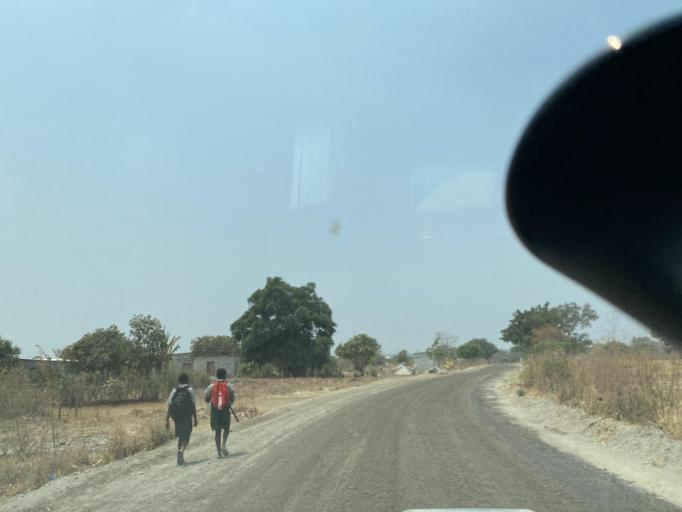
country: ZM
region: Lusaka
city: Lusaka
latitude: -15.5607
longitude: 28.4305
